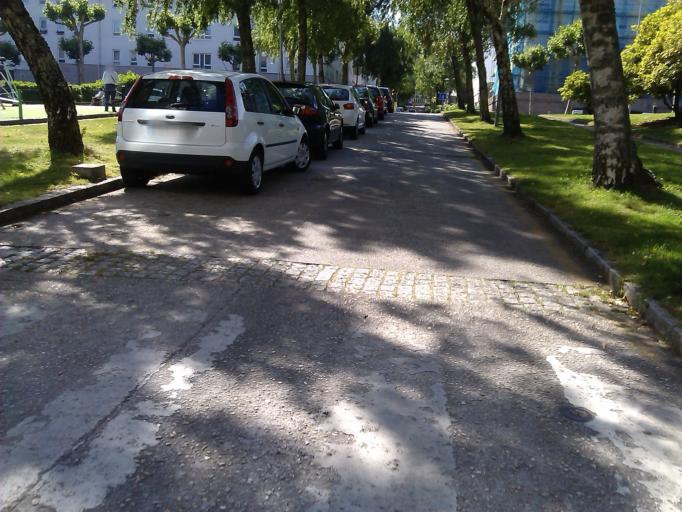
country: ES
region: Galicia
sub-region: Provincia da Coruna
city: Santiago de Compostela
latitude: 42.8822
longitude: -8.5294
